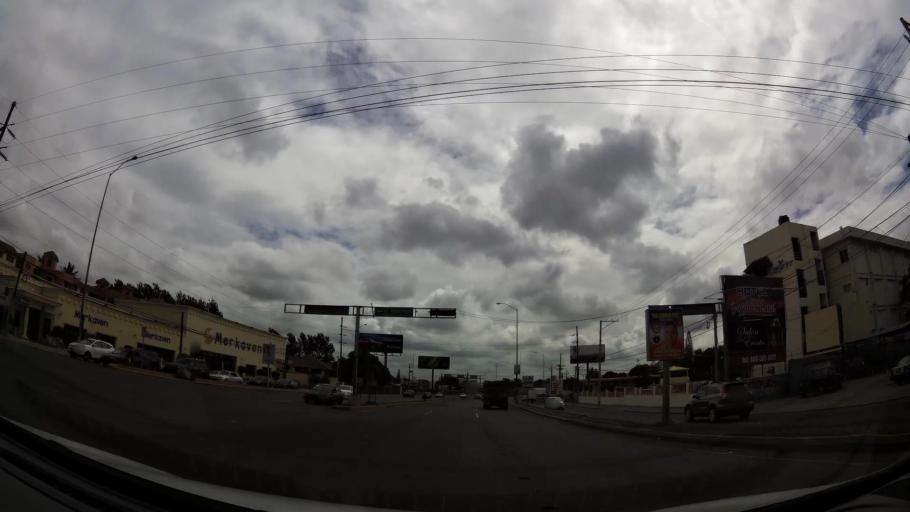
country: DO
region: Santiago
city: Santiago de los Caballeros
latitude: 19.4485
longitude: -70.6782
